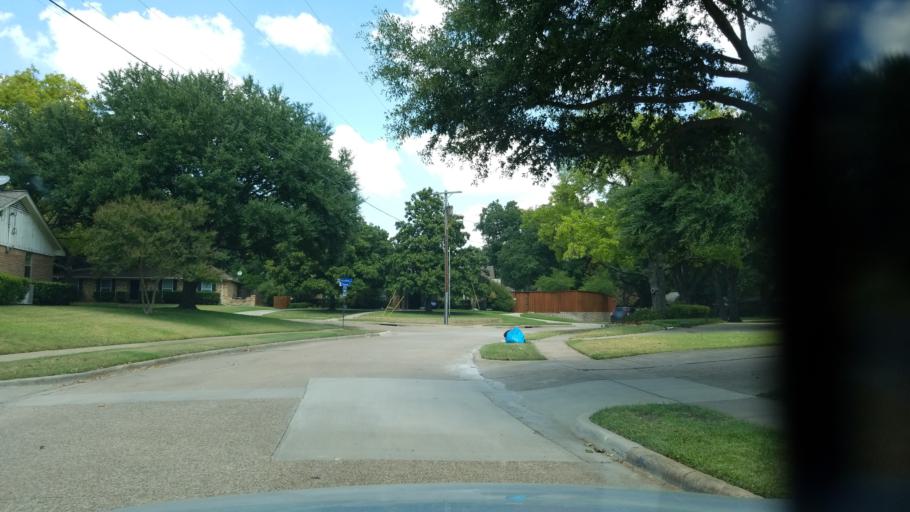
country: US
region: Texas
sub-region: Dallas County
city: Richardson
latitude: 32.9694
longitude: -96.7567
